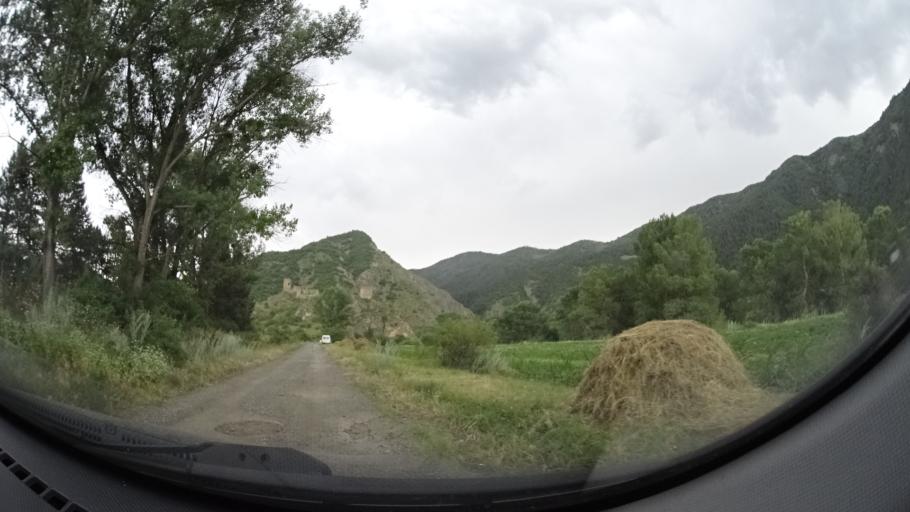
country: GE
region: Samtskhe-Javakheti
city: Aspindza
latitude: 41.7463
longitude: 43.2019
